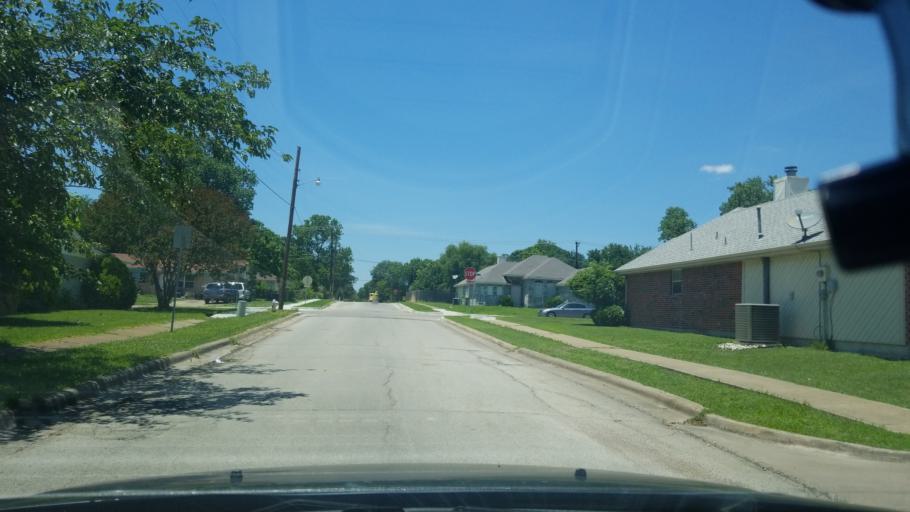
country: US
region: Texas
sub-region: Dallas County
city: Mesquite
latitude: 32.7784
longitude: -96.6067
